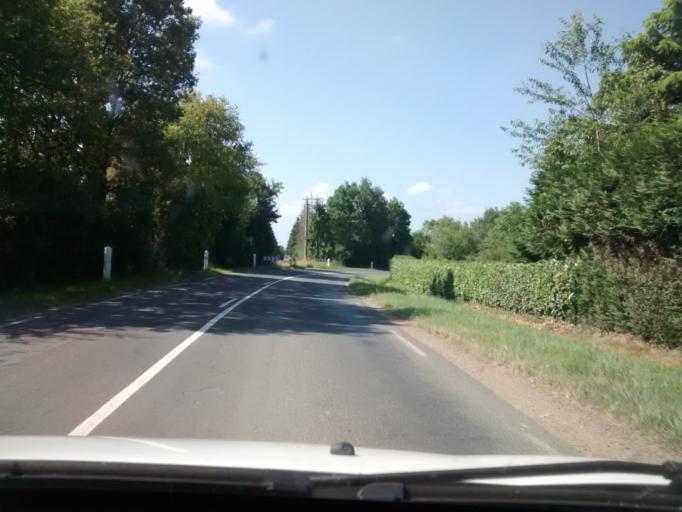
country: FR
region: Pays de la Loire
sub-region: Departement de la Sarthe
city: Saint-Calais
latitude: 47.9430
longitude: 0.7516
